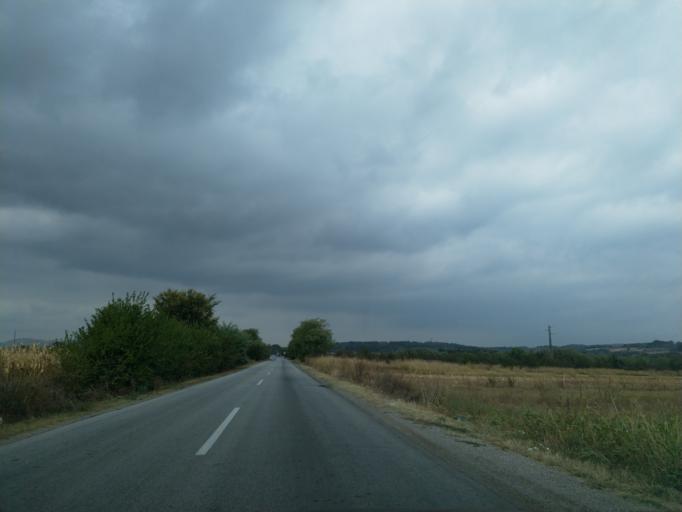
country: RS
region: Central Serbia
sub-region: Pomoravski Okrug
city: Jagodina
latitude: 43.9980
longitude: 21.2179
